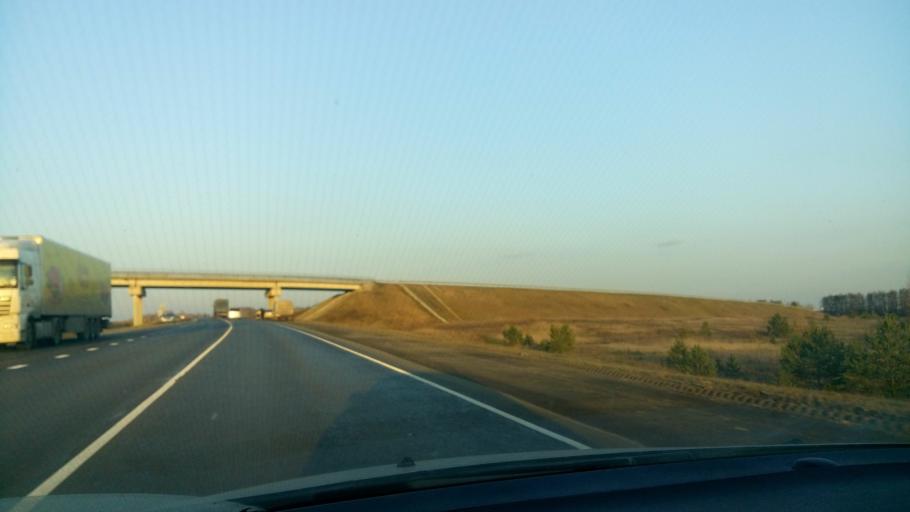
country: RU
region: Sverdlovsk
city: Yelanskiy
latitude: 56.7848
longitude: 62.5003
